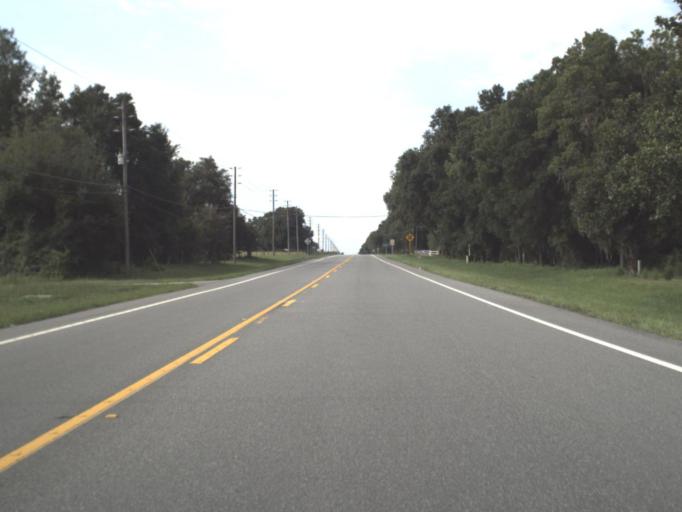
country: US
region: Florida
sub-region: Hernando County
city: Ridge Manor
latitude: 28.5039
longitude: -82.1954
